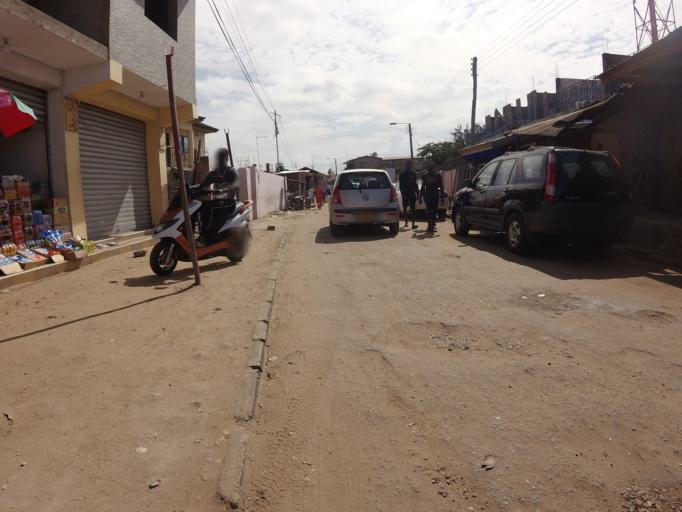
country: GH
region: Greater Accra
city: Accra
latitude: 5.5941
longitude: -0.1933
